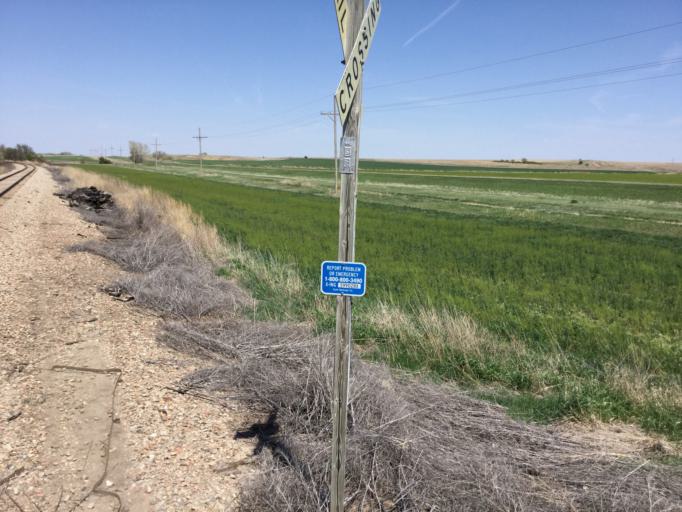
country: US
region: Kansas
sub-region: Decatur County
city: Oberlin
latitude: 39.6692
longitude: -100.3295
